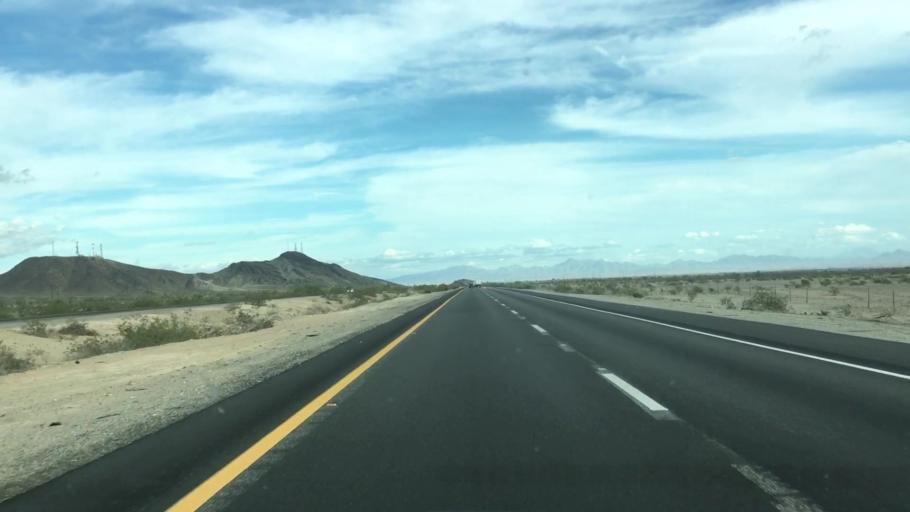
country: US
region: California
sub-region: Riverside County
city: Mesa Verde
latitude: 33.6098
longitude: -114.7949
